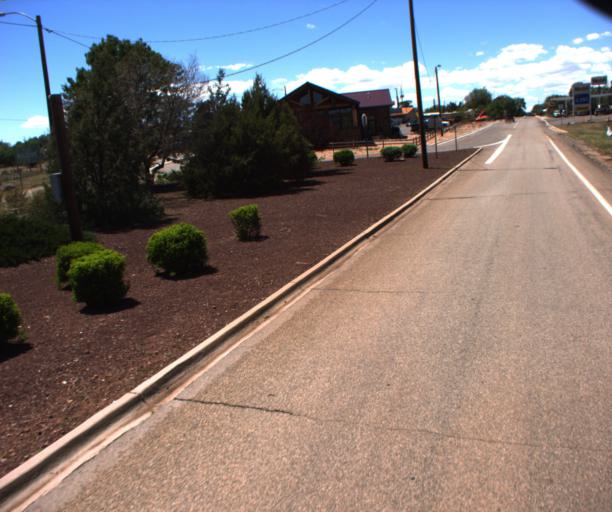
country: US
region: Arizona
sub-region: Coconino County
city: Williams
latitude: 35.2229
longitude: -112.4773
